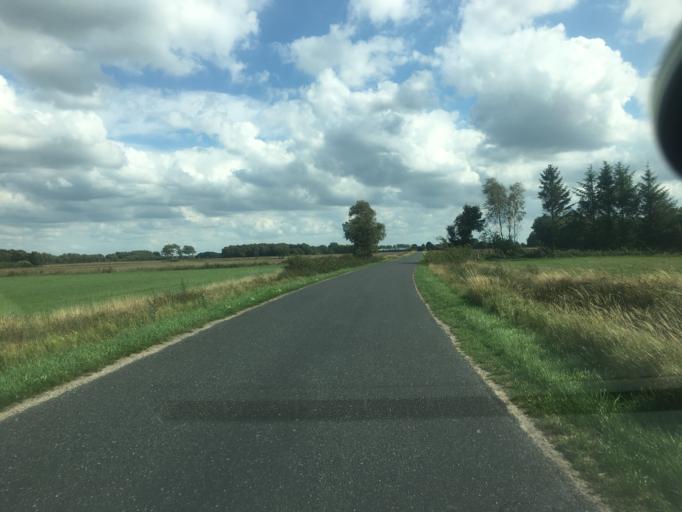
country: DK
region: South Denmark
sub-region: Tonder Kommune
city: Logumkloster
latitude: 55.0200
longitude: 8.9904
